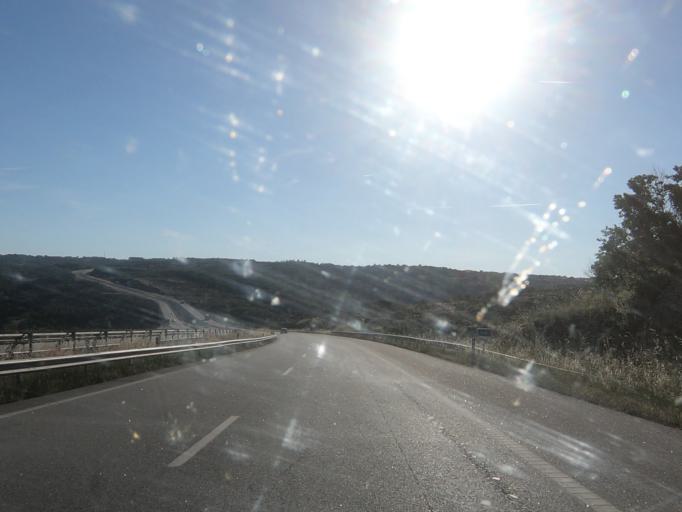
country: ES
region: Castille and Leon
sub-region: Provincia de Salamanca
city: Fuentes de Onoro
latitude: 40.6114
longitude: -6.9109
